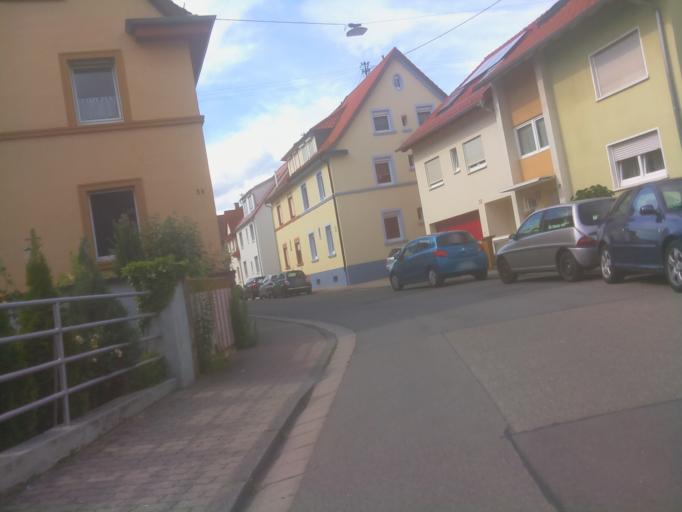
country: DE
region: Baden-Wuerttemberg
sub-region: Karlsruhe Region
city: Dossenheim
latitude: 49.4481
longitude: 8.6722
